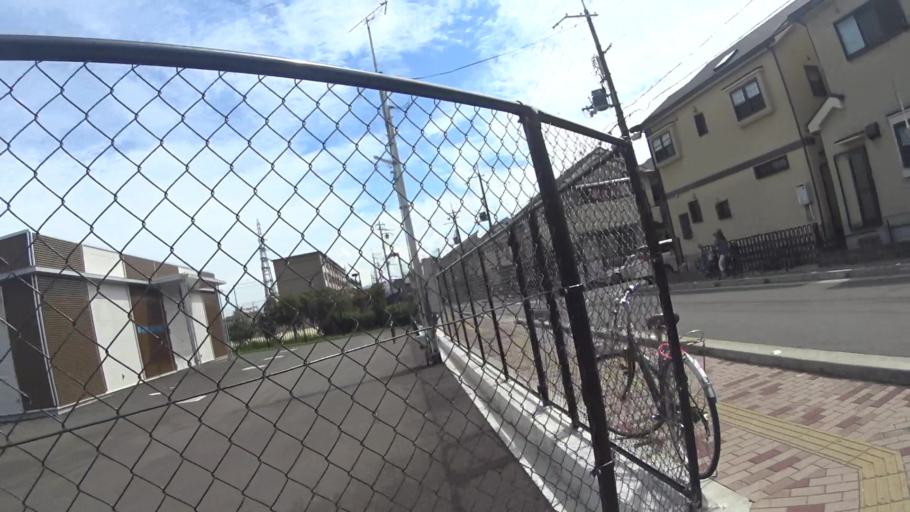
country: JP
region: Kyoto
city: Muko
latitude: 34.9598
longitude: 135.7064
